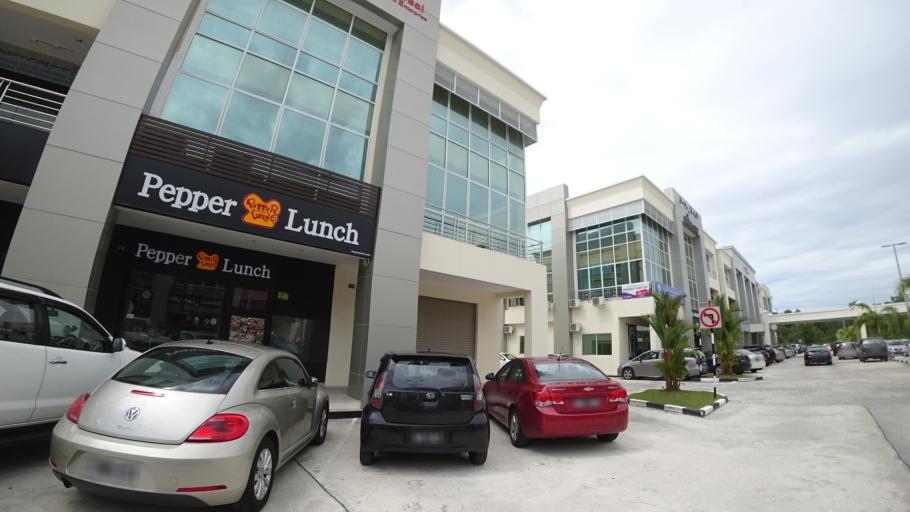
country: BN
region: Brunei and Muara
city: Bandar Seri Begawan
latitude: 4.9043
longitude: 114.9223
